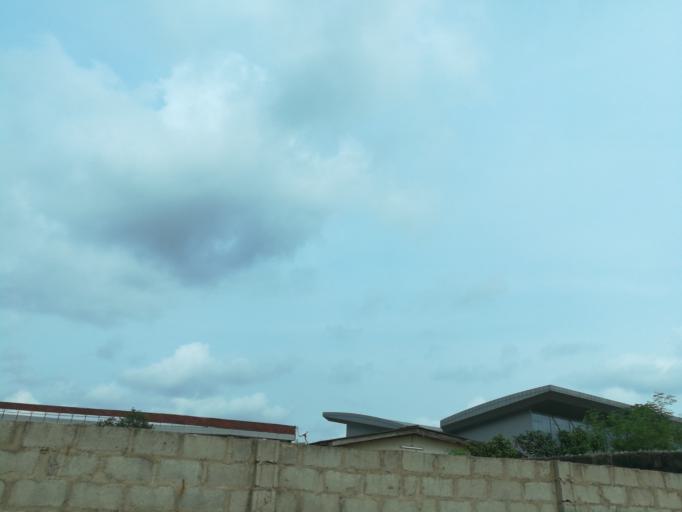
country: NG
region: Lagos
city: Oshodi
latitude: 6.5757
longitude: 3.3245
